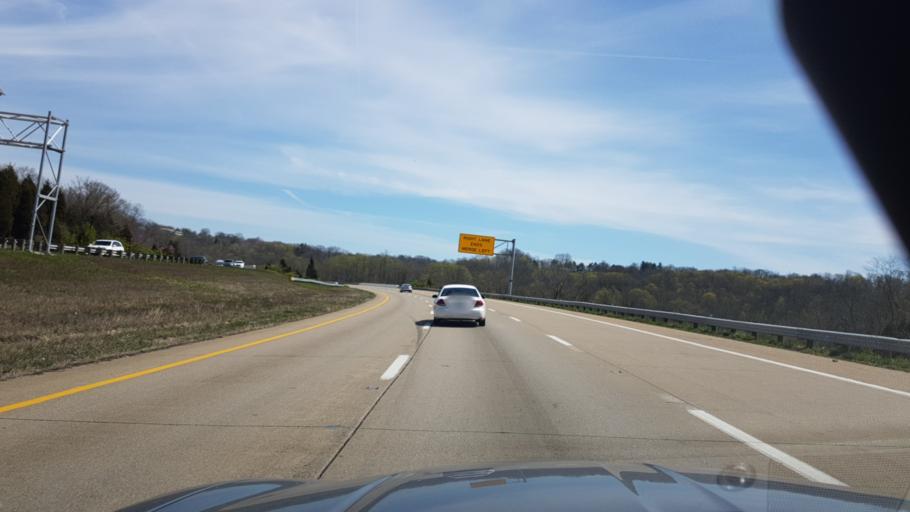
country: US
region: Kentucky
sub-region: Campbell County
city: Silver Grove
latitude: 39.0545
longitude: -84.3942
